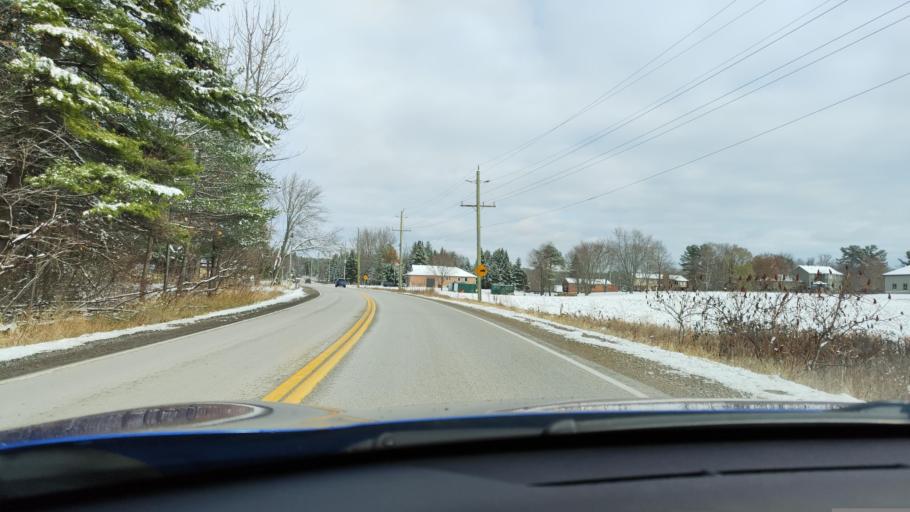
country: CA
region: Ontario
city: Barrie
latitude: 44.3787
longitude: -79.7685
